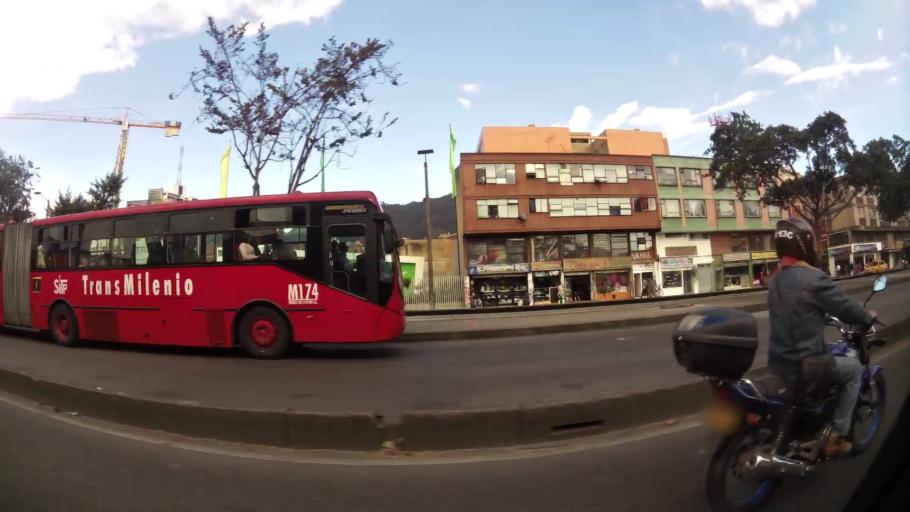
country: CO
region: Bogota D.C.
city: Bogota
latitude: 4.6451
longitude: -74.0656
